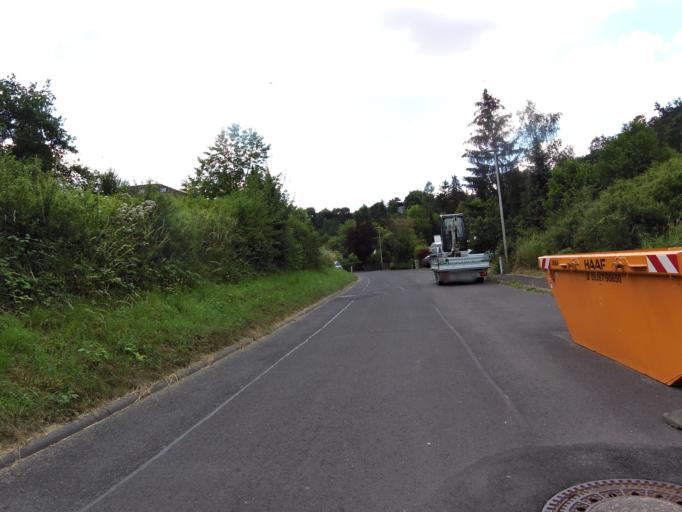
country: DE
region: Bavaria
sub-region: Regierungsbezirk Unterfranken
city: Gadheim
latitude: 49.8330
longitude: 9.9193
